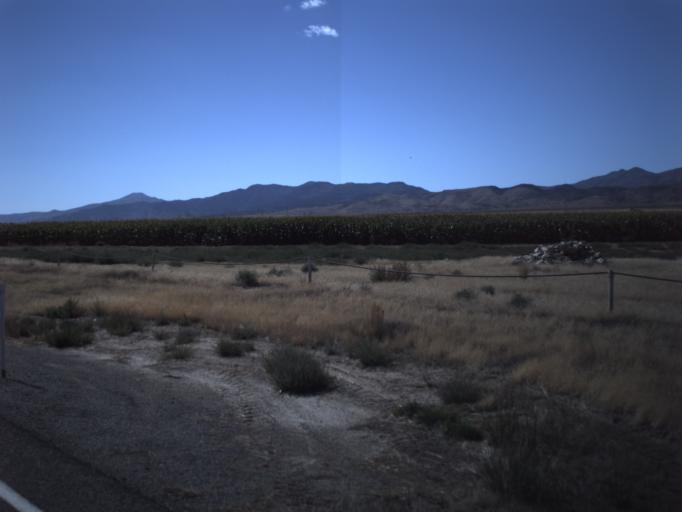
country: US
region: Utah
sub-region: Utah County
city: Genola
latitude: 40.0138
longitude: -111.9583
